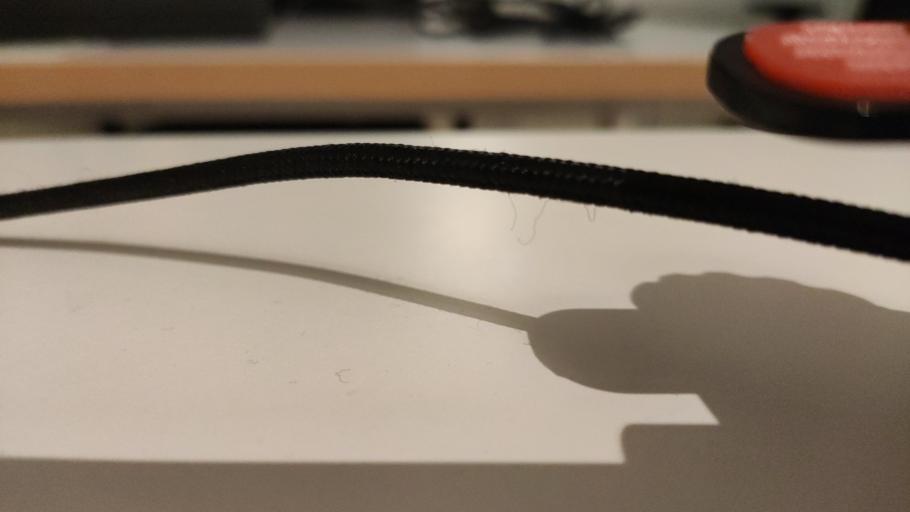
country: RU
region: Moskovskaya
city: Novosin'kovo
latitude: 56.3736
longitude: 37.3383
